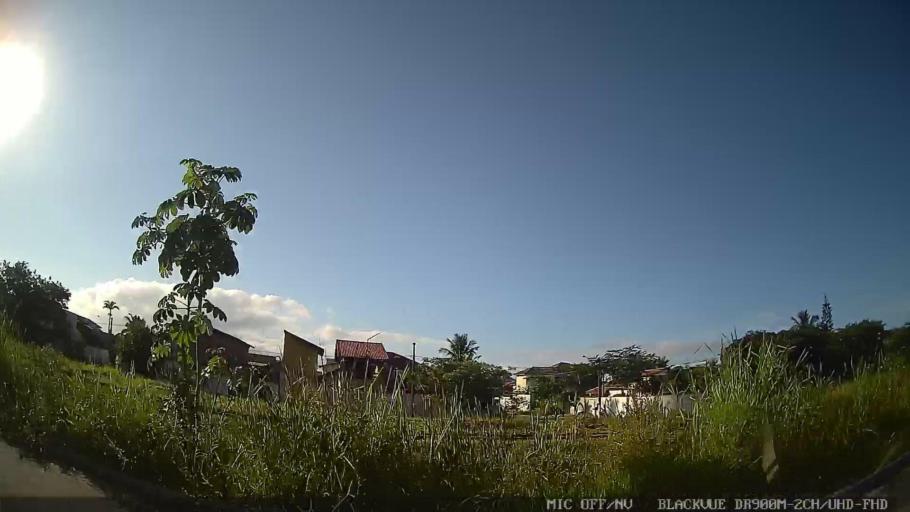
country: BR
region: Sao Paulo
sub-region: Peruibe
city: Peruibe
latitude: -24.2900
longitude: -46.9722
